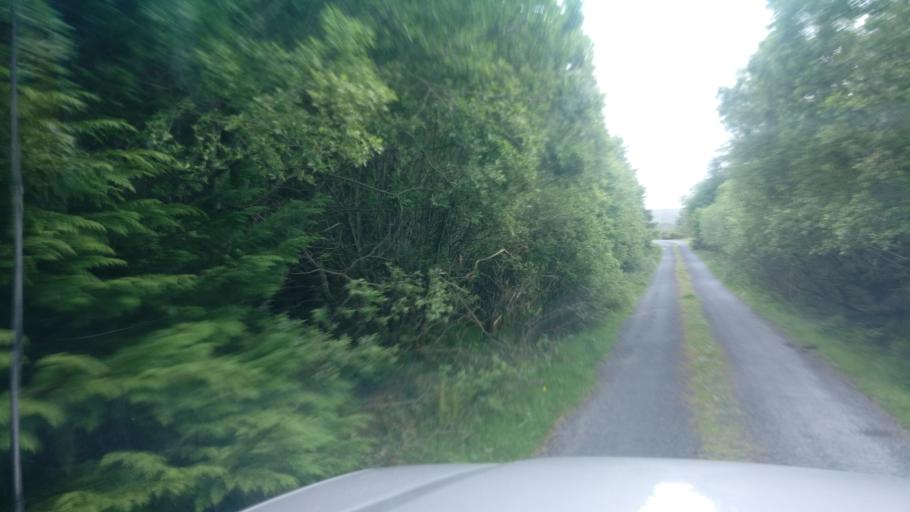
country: IE
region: Connaught
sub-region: County Galway
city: Loughrea
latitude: 53.1130
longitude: -8.6738
